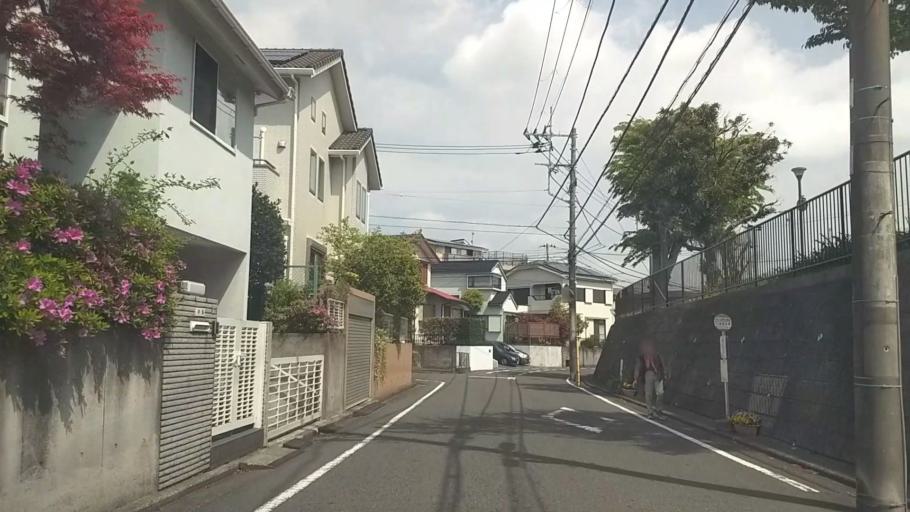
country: JP
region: Kanagawa
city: Yokohama
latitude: 35.3892
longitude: 139.5914
